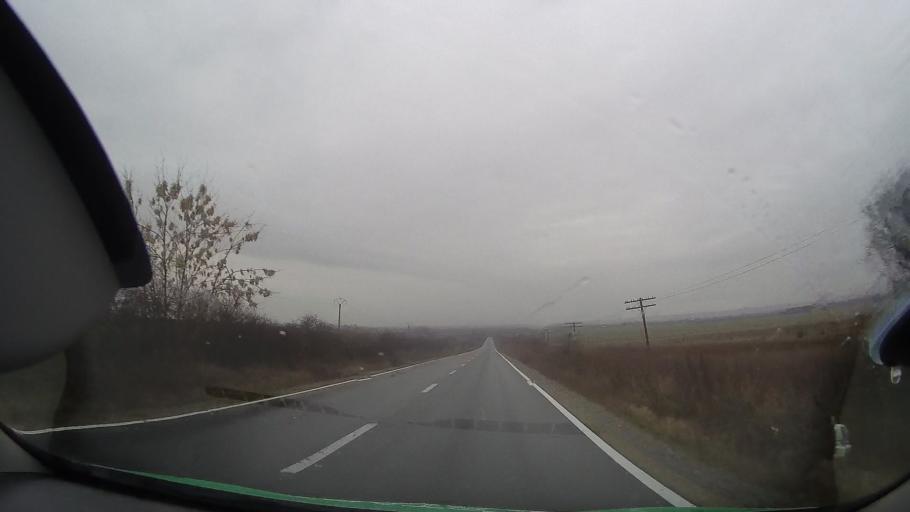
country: RO
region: Bihor
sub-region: Comuna Olcea
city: Calacea
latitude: 46.7180
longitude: 21.9528
